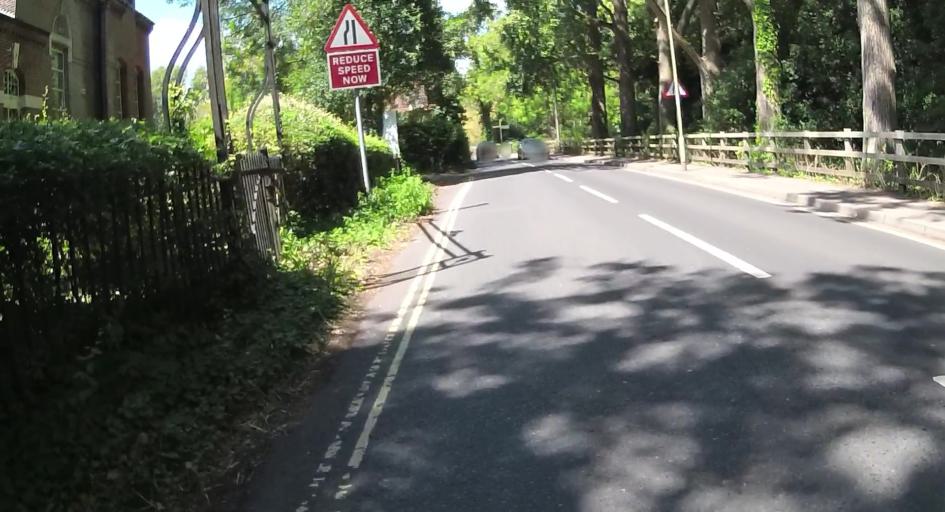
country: GB
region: England
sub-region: Hampshire
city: Winchester
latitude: 51.0515
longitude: -1.3166
